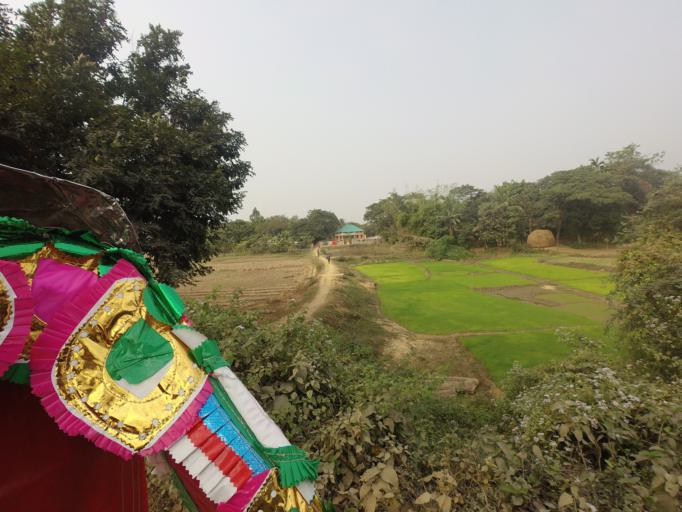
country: BD
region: Dhaka
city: Netrakona
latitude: 25.1076
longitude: 90.6585
